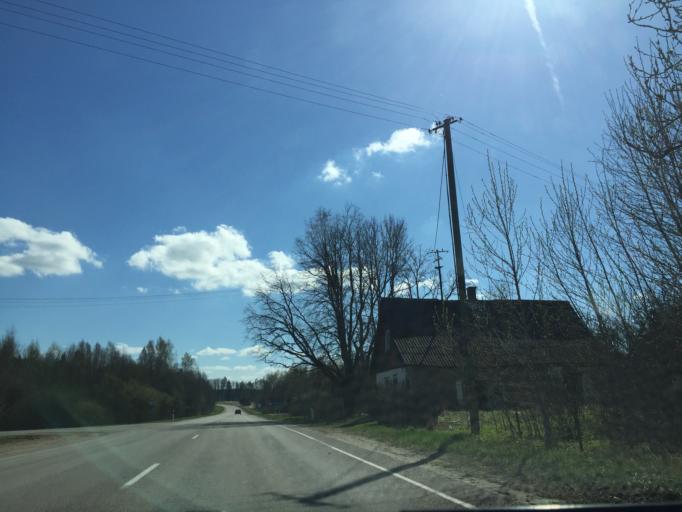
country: EE
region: Valgamaa
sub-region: Valga linn
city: Valga
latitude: 57.8709
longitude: 26.0593
